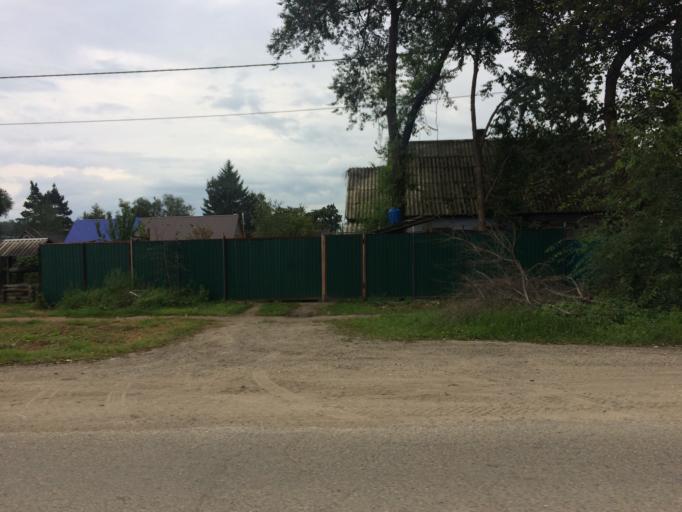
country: RU
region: Primorskiy
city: Dal'nerechensk
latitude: 45.9312
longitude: 133.7593
